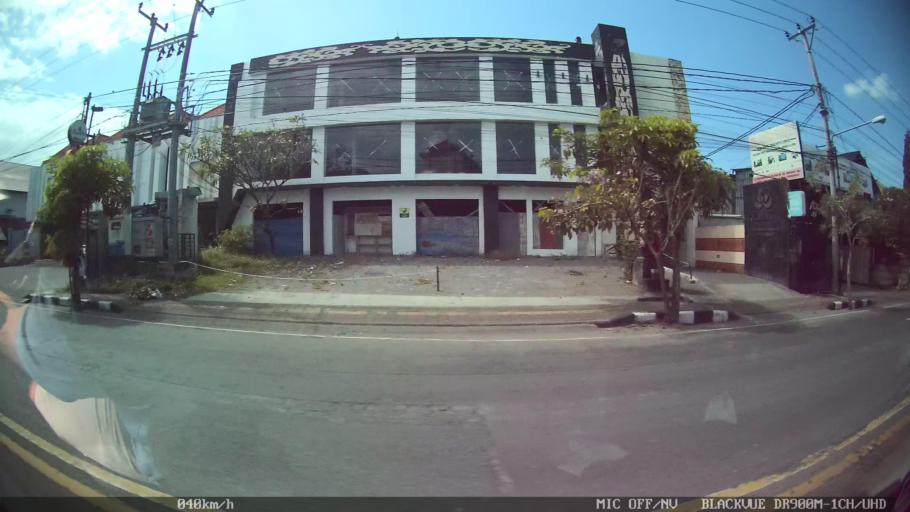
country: ID
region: Bali
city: Karyadharma
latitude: -8.6832
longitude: 115.1883
